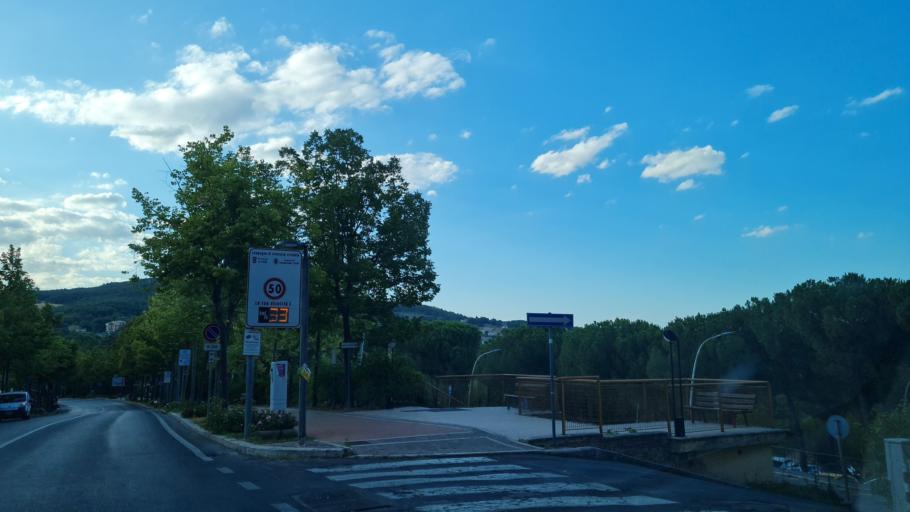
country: IT
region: Tuscany
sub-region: Provincia di Siena
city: Chianciano Terme
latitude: 43.0379
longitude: 11.8212
